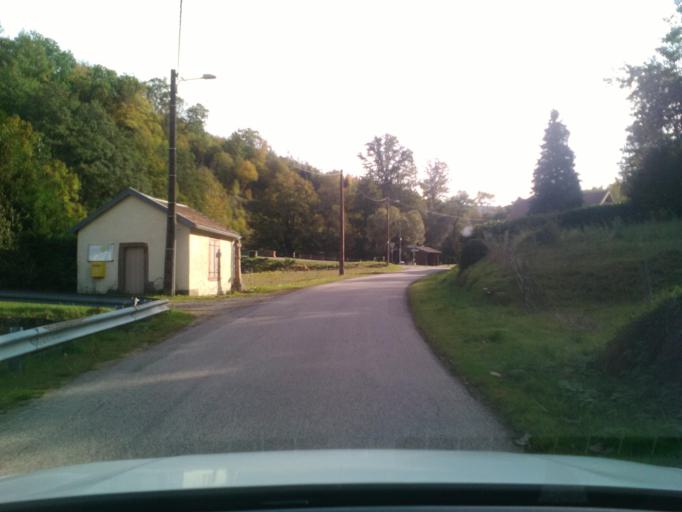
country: FR
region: Lorraine
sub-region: Departement des Vosges
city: Senones
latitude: 48.3742
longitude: 7.0542
